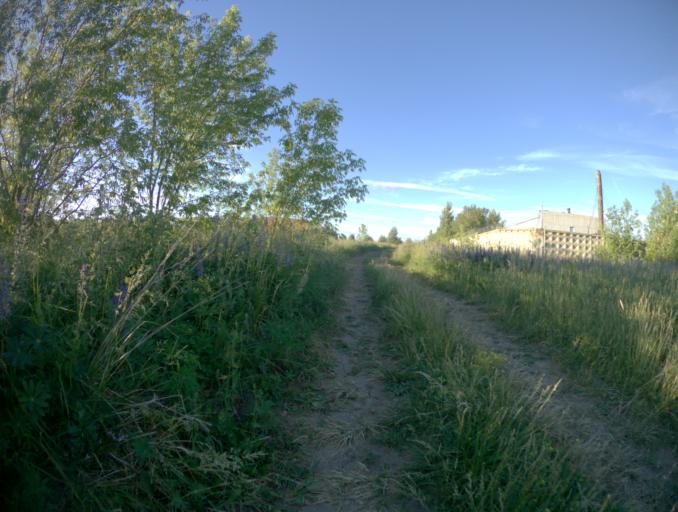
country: RU
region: Vladimir
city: Bogolyubovo
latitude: 56.1868
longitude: 40.5107
